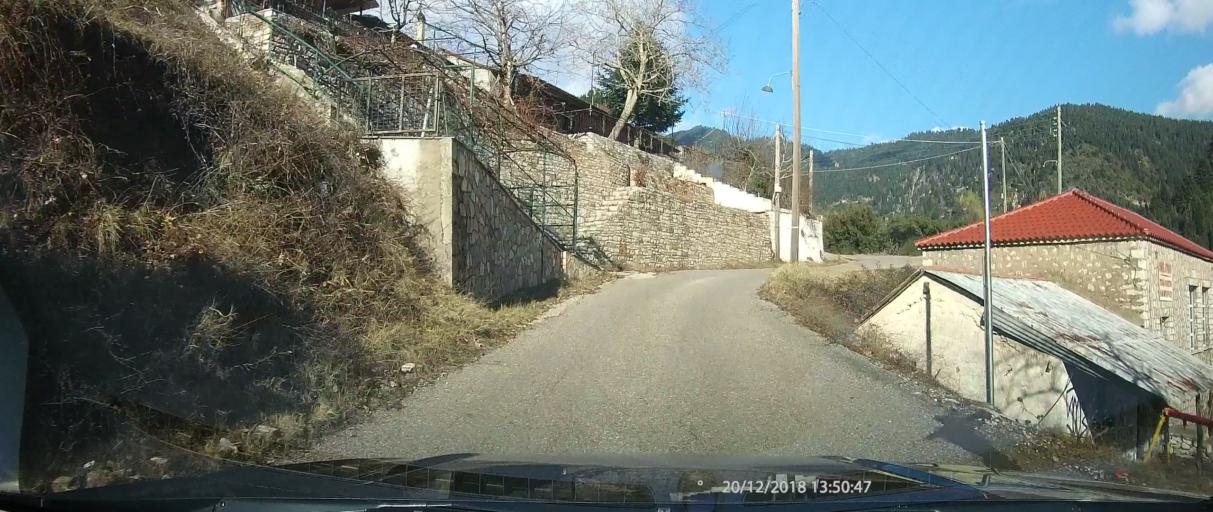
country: GR
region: West Greece
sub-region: Nomos Aitolias kai Akarnanias
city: Paravola
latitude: 38.7000
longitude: 21.6047
